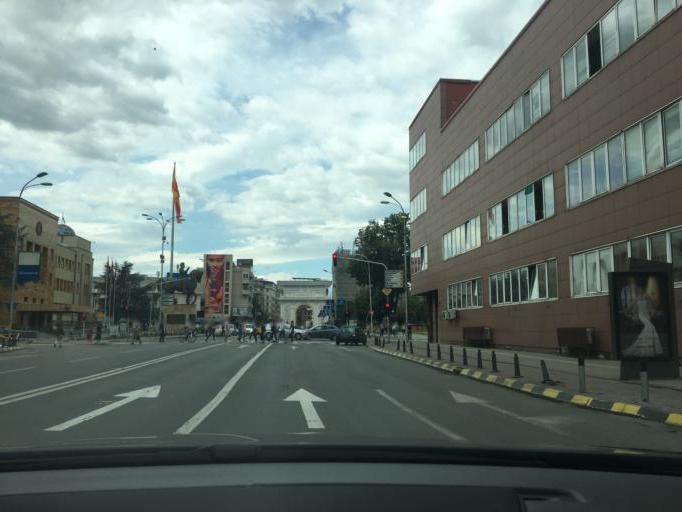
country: MK
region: Karpos
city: Skopje
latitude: 41.9923
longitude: 21.4340
